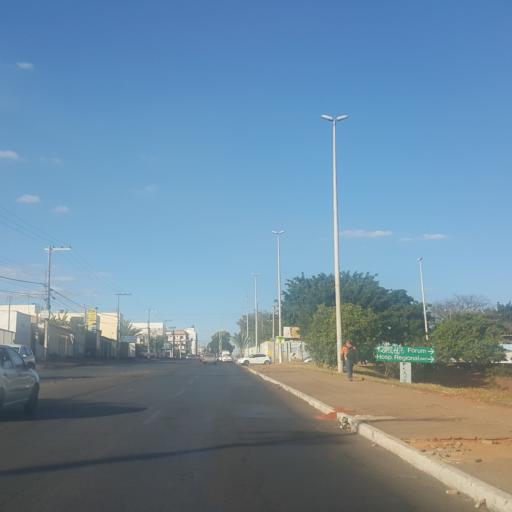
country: BR
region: Federal District
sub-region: Brasilia
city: Brasilia
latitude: -15.8191
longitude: -48.0679
